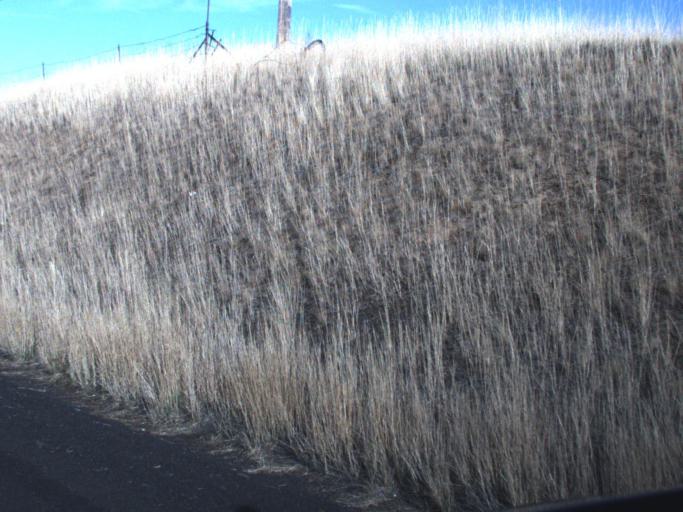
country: US
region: Washington
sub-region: Lincoln County
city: Davenport
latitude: 47.8463
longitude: -118.2133
